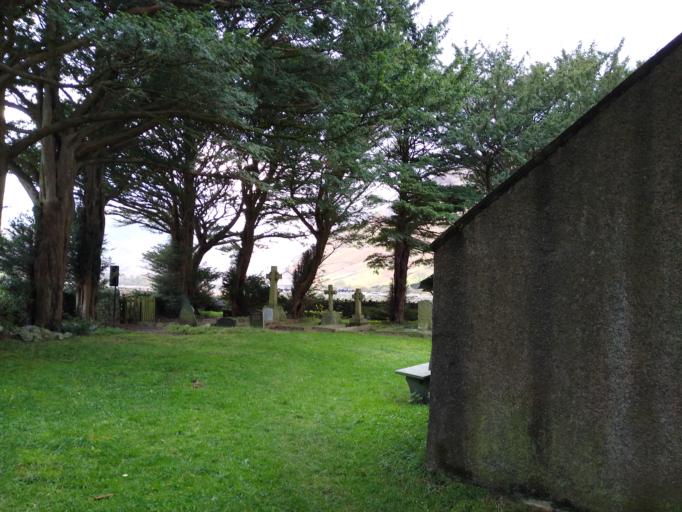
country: GB
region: England
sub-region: Cumbria
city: Keswick
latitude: 54.4672
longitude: -3.2533
